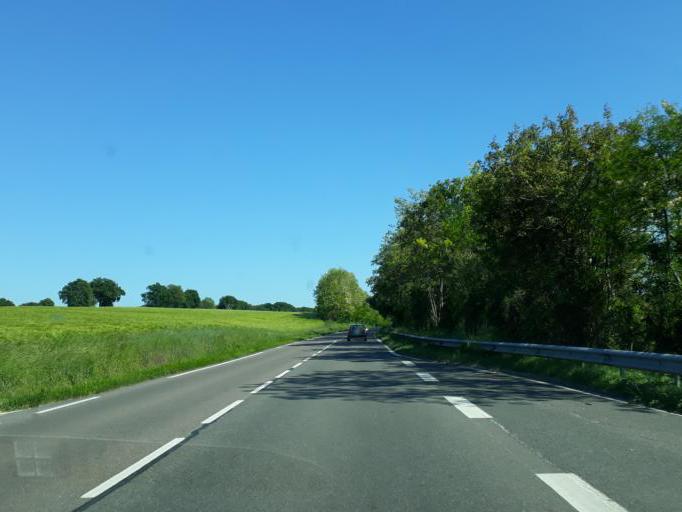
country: FR
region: Bourgogne
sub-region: Departement de la Nievre
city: Neuvy-sur-Loire
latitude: 47.5041
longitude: 2.9027
